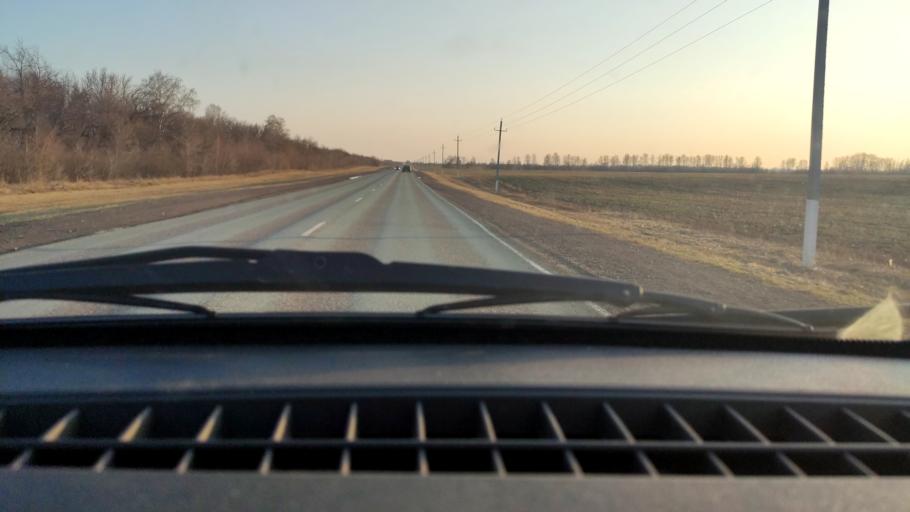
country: RU
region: Bashkortostan
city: Davlekanovo
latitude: 54.3145
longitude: 55.1485
